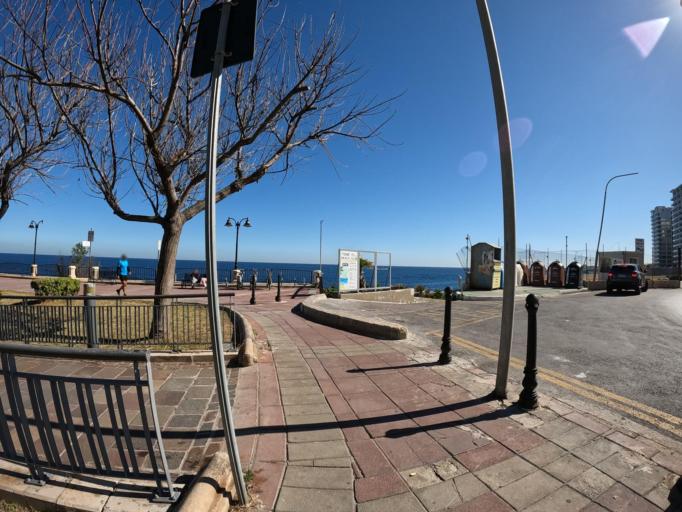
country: MT
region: Tas-Sliema
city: Sliema
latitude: 35.9100
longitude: 14.5102
